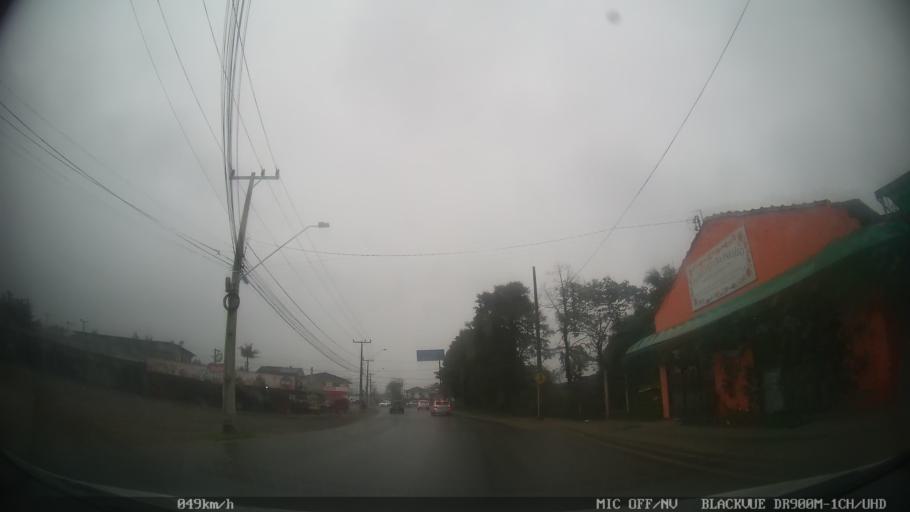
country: BR
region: Santa Catarina
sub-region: Joinville
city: Joinville
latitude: -26.2185
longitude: -48.8189
